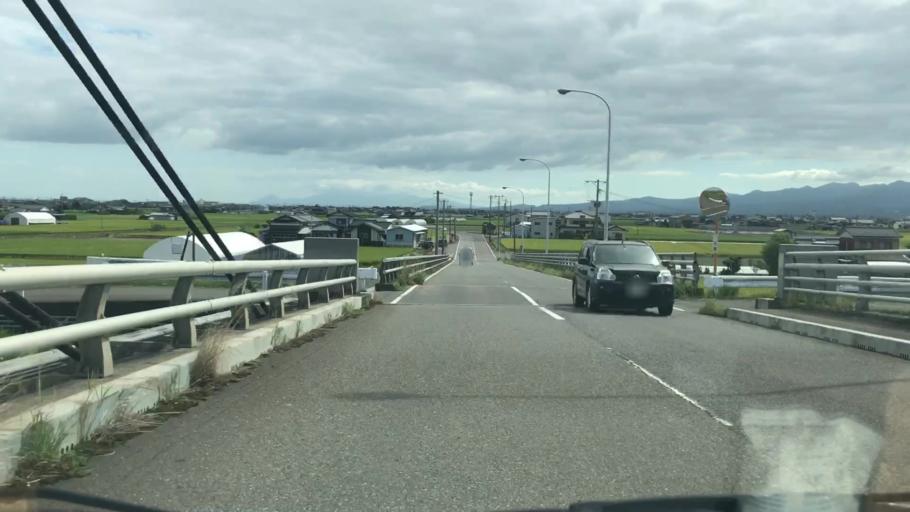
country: JP
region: Saga Prefecture
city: Saga-shi
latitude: 33.1993
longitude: 130.1813
